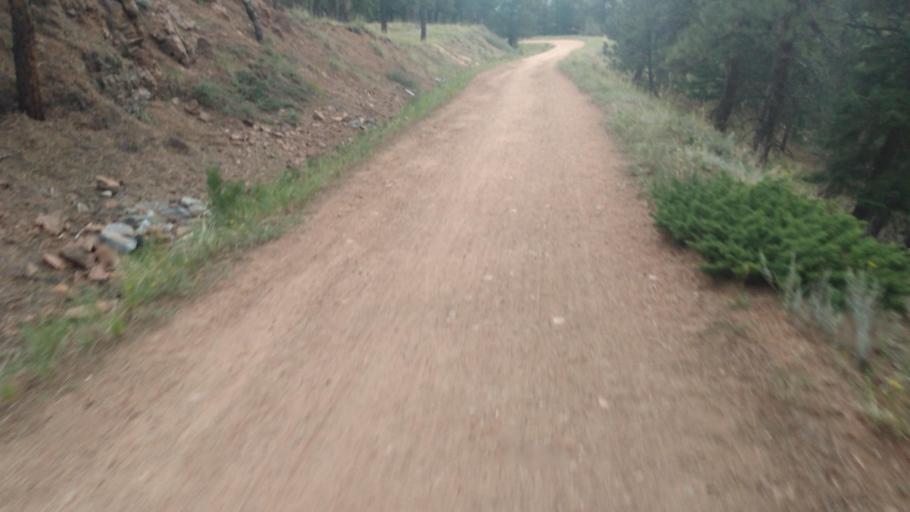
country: US
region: Colorado
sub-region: Boulder County
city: Boulder
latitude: 39.9983
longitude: -105.3143
